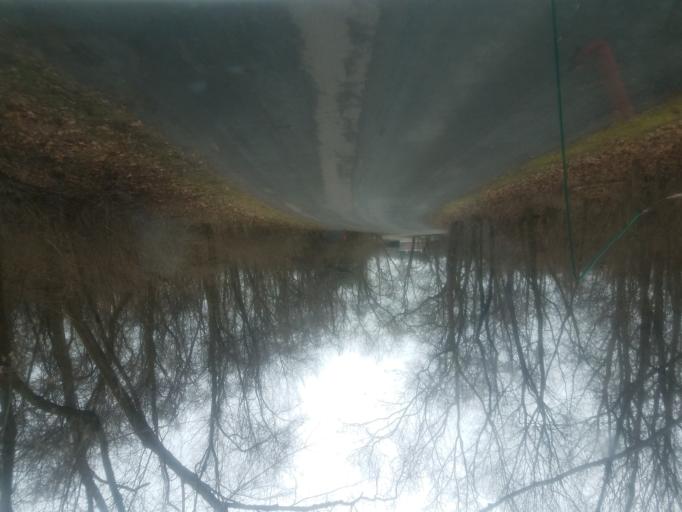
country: US
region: Ohio
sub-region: Franklin County
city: Westerville
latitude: 40.1296
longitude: -82.9463
